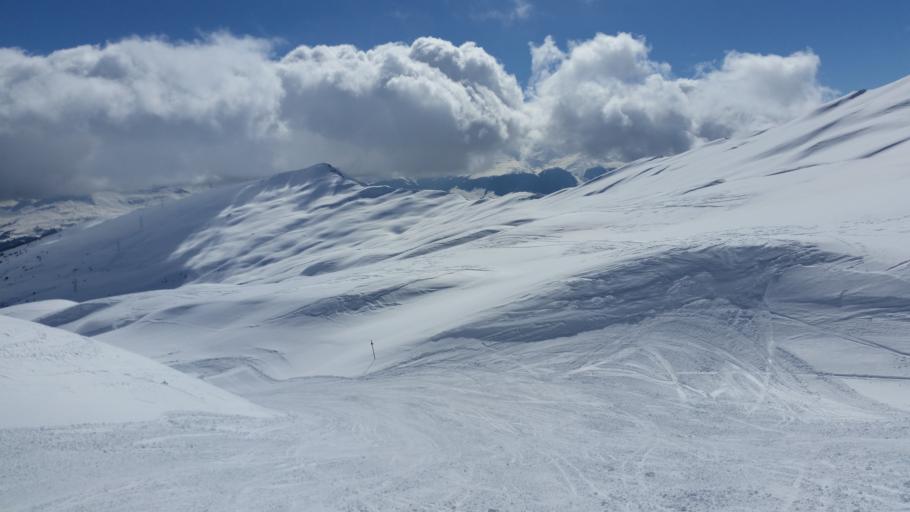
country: CH
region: Grisons
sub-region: Surselva District
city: Ilanz
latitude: 46.8577
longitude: 9.1530
